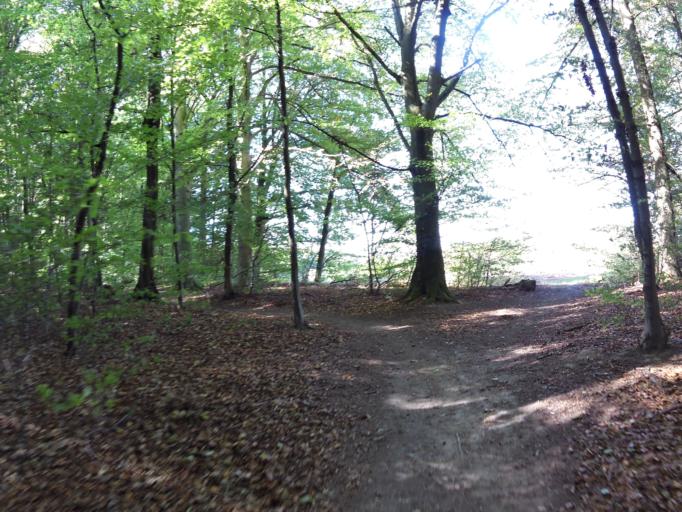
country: DE
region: Bavaria
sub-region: Regierungsbezirk Unterfranken
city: Eisingen
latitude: 49.7690
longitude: 9.8442
